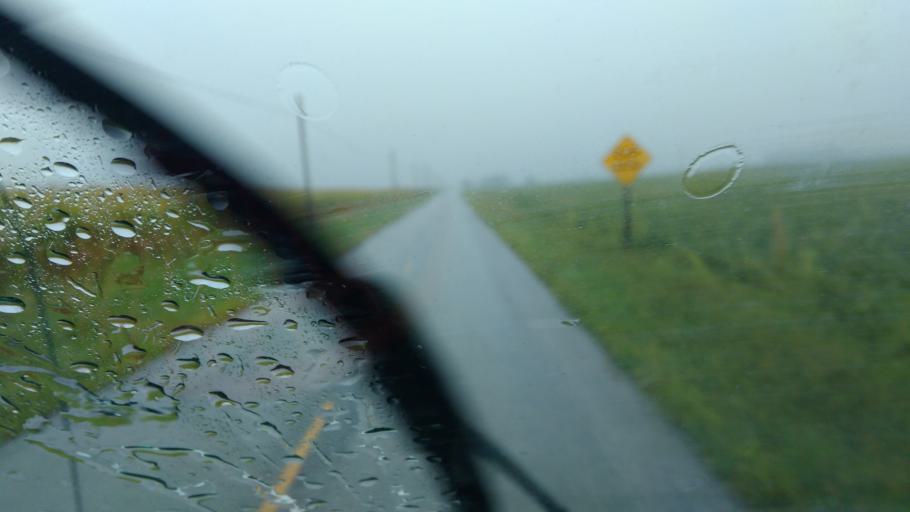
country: US
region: Ohio
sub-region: Hardin County
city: Kenton
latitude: 40.7030
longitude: -83.5948
